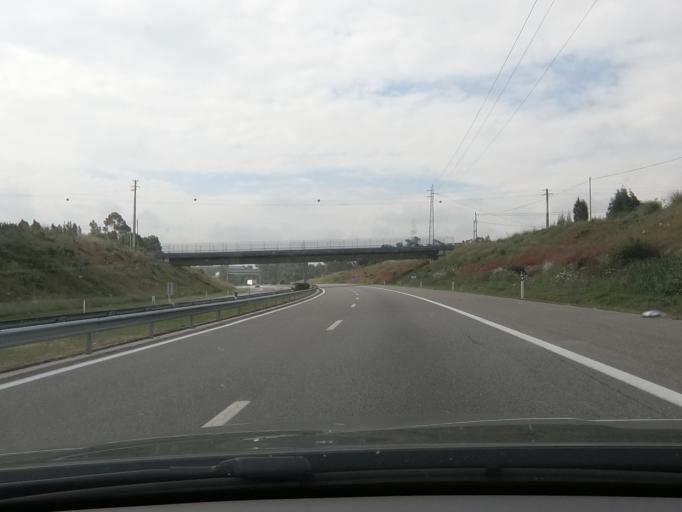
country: PT
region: Aveiro
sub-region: Aveiro
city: Oliveirinha
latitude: 40.6331
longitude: -8.6032
